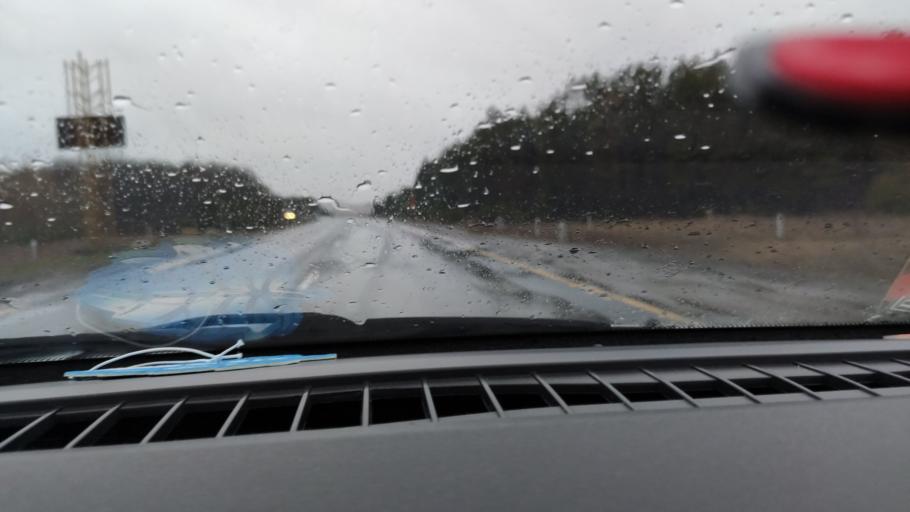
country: RU
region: Tatarstan
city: Mendeleyevsk
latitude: 55.9458
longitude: 52.2963
